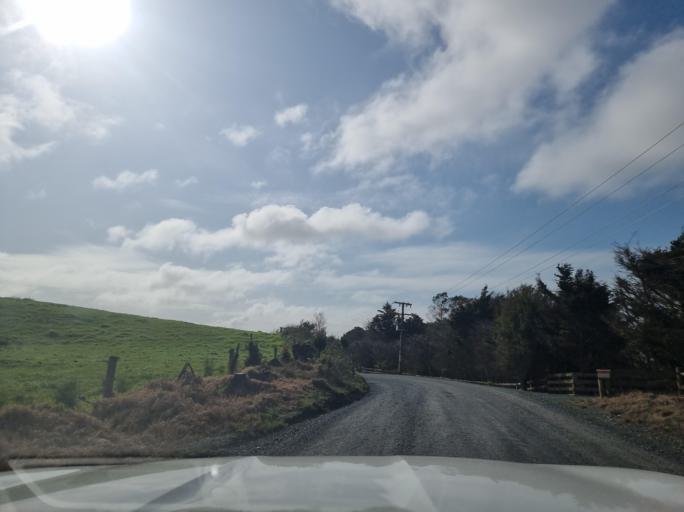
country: NZ
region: Northland
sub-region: Whangarei
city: Ruakaka
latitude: -36.0130
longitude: 174.4683
